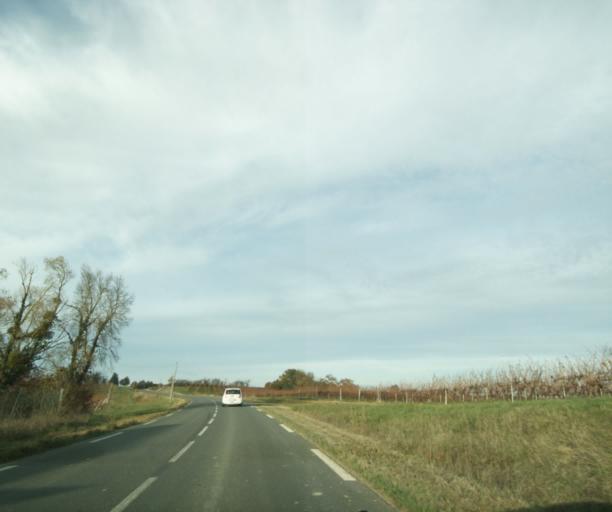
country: FR
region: Midi-Pyrenees
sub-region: Departement du Gers
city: Eauze
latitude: 43.8079
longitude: 0.0964
